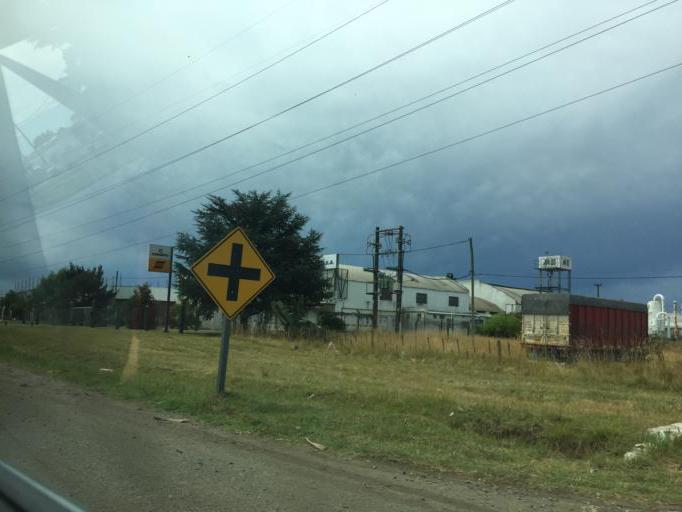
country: AR
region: Buenos Aires
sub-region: Partido de Tandil
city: Tandil
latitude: -37.2977
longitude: -59.1318
